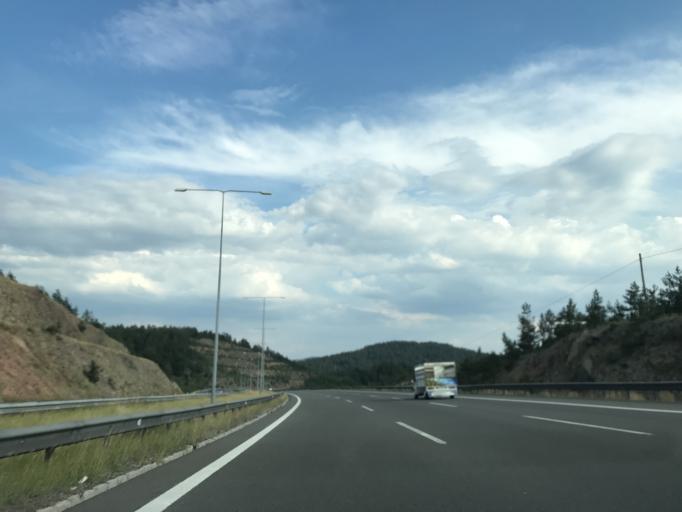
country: TR
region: Ankara
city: Pecenek
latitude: 40.5729
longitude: 32.3036
